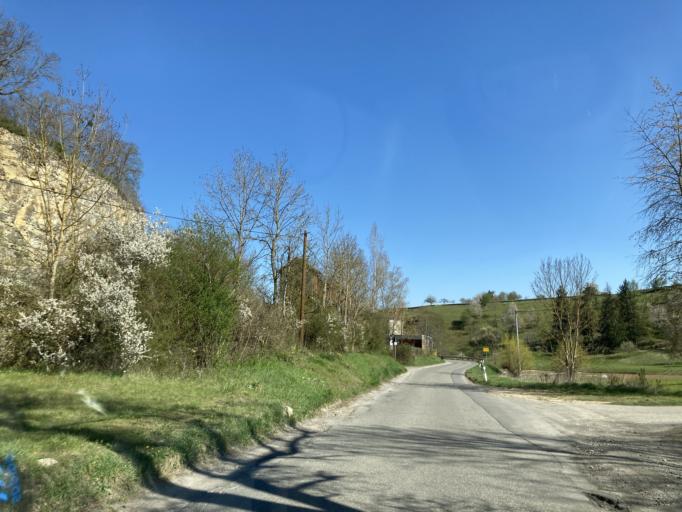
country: DE
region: Baden-Wuerttemberg
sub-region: Tuebingen Region
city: Rottenburg
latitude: 48.5405
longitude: 8.9172
